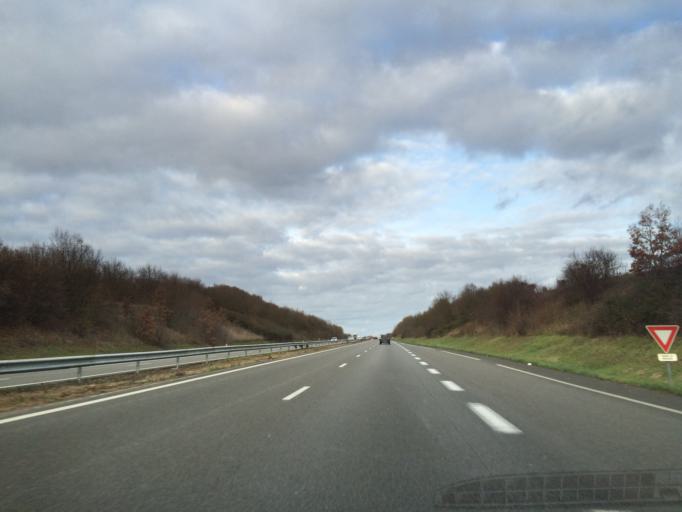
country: FR
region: Poitou-Charentes
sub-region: Departement de la Charente-Maritime
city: Saint-Jean-d'Angely
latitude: 45.9713
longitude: -0.5482
